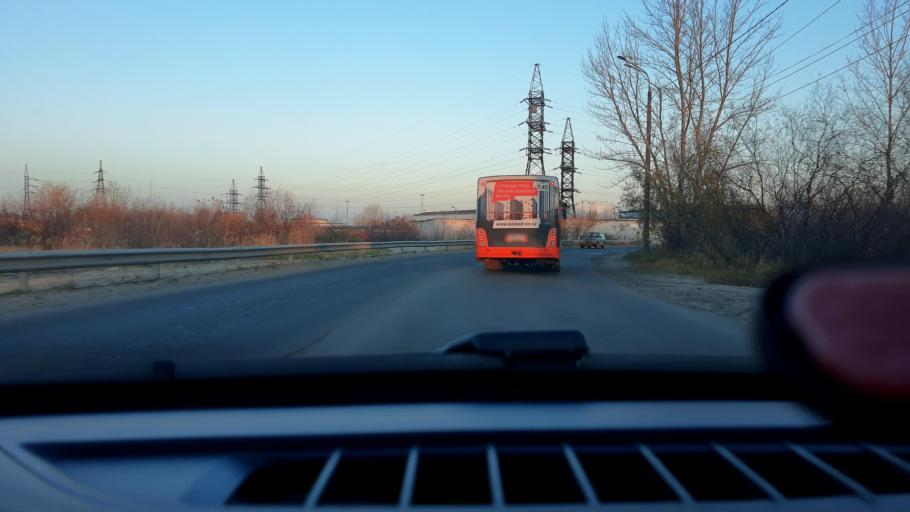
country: RU
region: Nizjnij Novgorod
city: Gorbatovka
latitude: 56.3609
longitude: 43.7942
